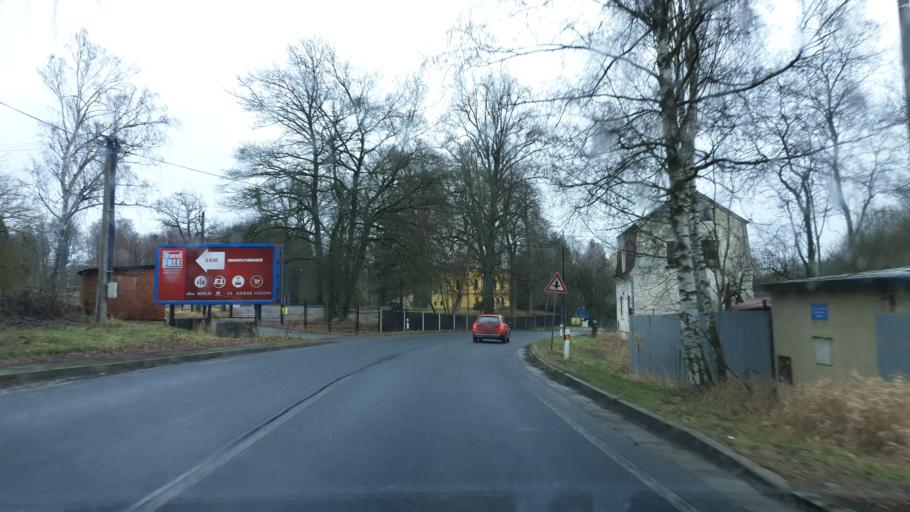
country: CZ
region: Karlovarsky
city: As
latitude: 50.2387
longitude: 12.1856
